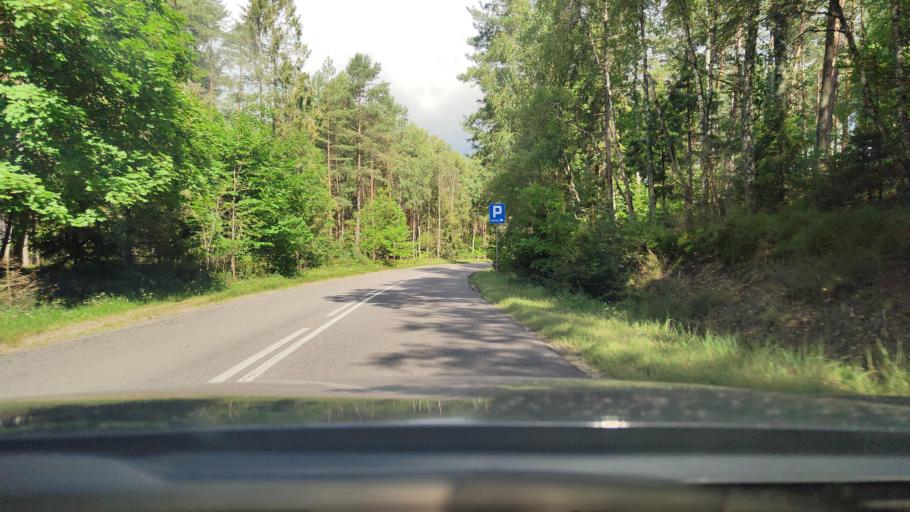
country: PL
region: Pomeranian Voivodeship
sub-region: Powiat wejherowski
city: Orle
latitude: 54.6469
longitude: 18.2139
